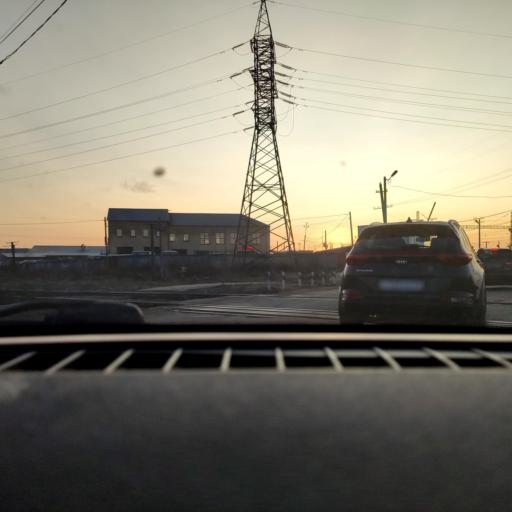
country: RU
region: Perm
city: Froly
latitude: 57.9538
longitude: 56.2458
